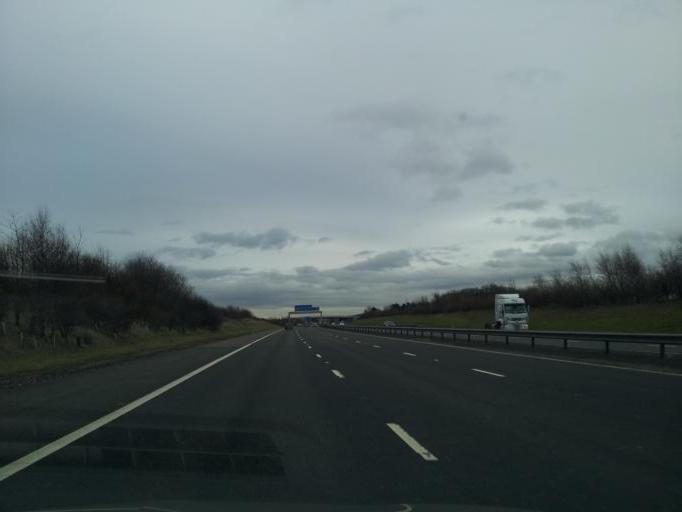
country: GB
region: England
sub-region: Staffordshire
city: Shenstone
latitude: 52.6450
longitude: -1.8250
